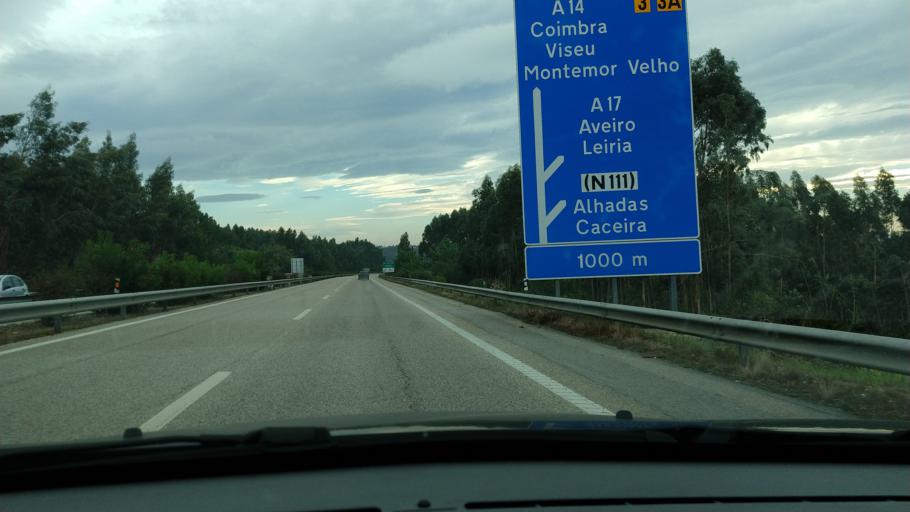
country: PT
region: Coimbra
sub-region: Figueira da Foz
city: Alhadas
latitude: 40.1530
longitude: -8.8067
